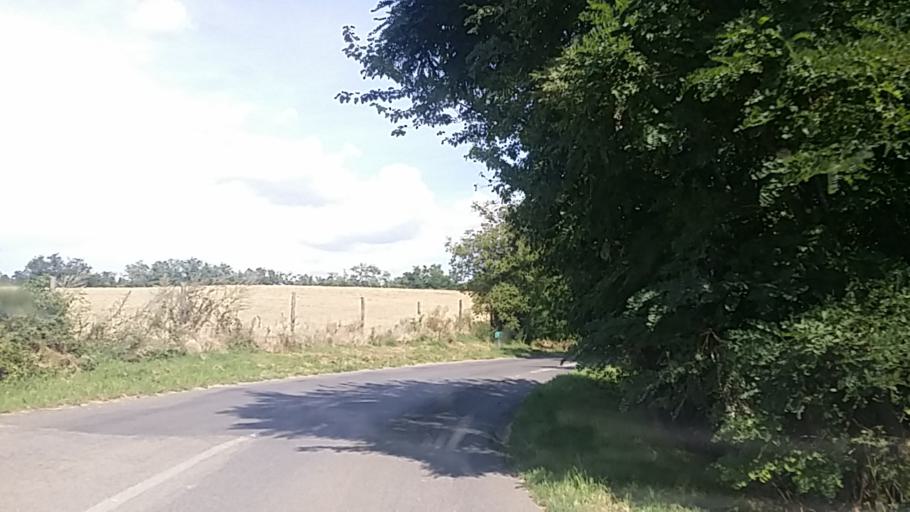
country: HU
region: Tolna
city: Hogyesz
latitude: 46.5218
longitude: 18.4181
